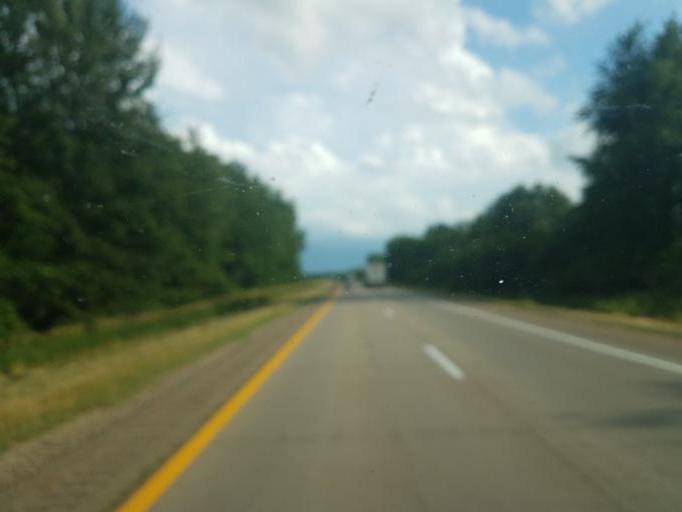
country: US
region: Michigan
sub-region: Calhoun County
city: Marshall
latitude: 42.1832
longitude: -84.9847
